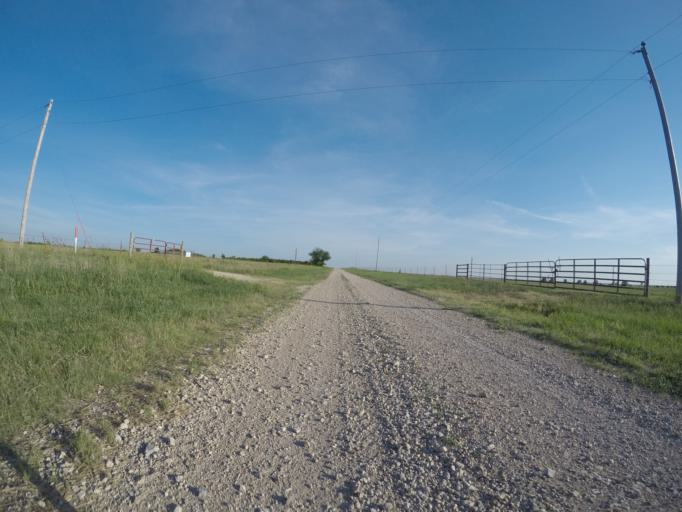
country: US
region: Kansas
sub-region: Riley County
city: Manhattan
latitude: 39.0016
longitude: -96.4920
